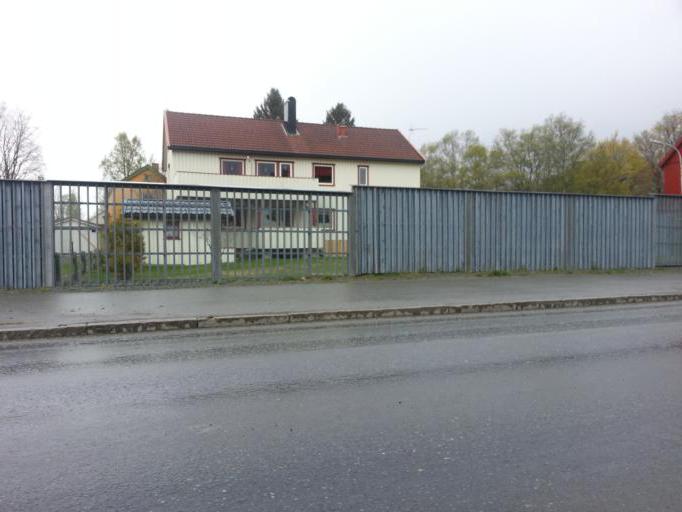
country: NO
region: Sor-Trondelag
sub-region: Trondheim
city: Trondheim
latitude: 63.3946
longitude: 10.3589
